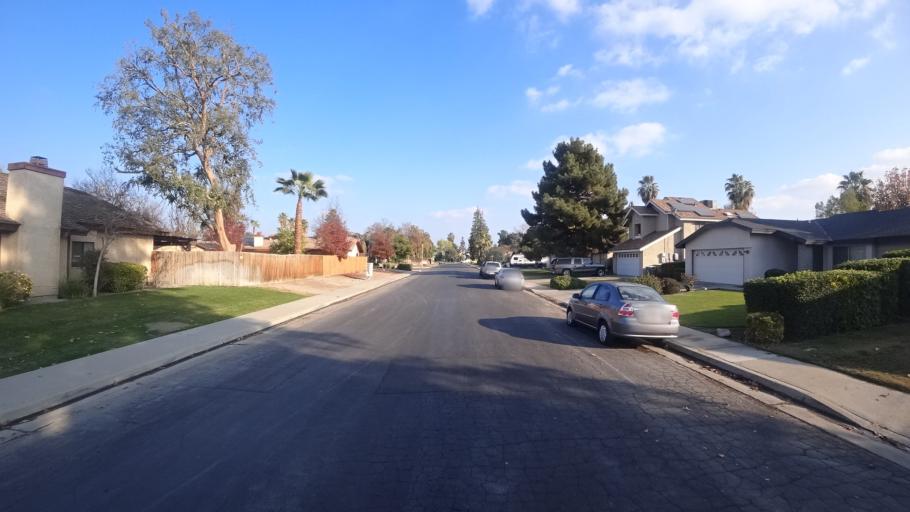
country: US
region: California
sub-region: Kern County
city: Greenacres
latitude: 35.3156
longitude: -119.0957
